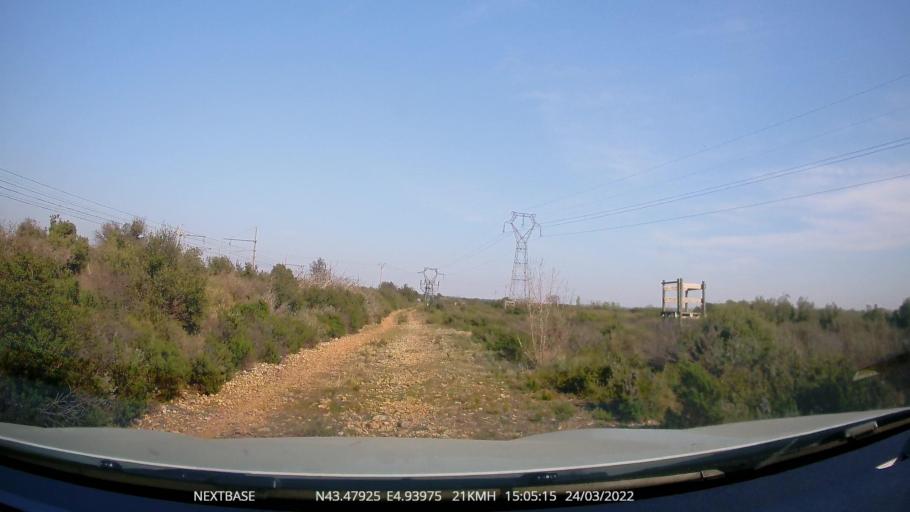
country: FR
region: Provence-Alpes-Cote d'Azur
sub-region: Departement des Bouches-du-Rhone
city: Fos-sur-Mer
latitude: 43.4794
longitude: 4.9400
